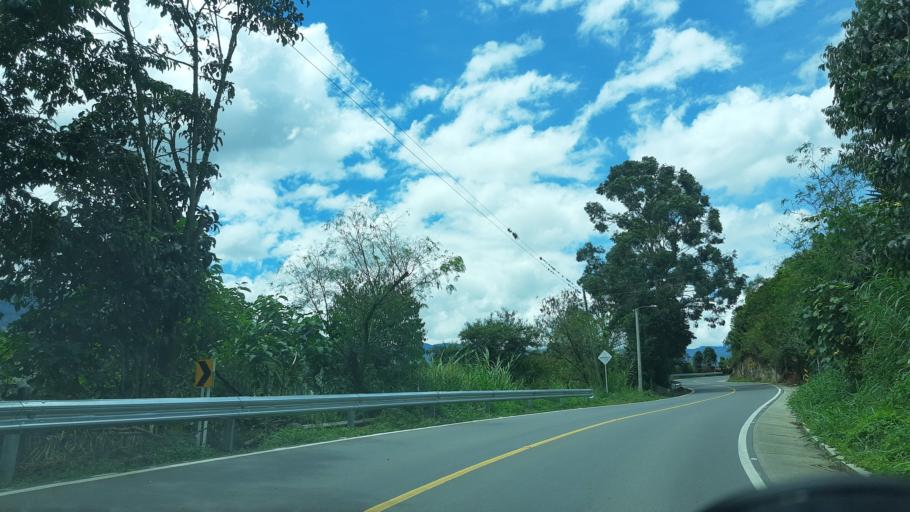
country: CO
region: Boyaca
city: Somondoco
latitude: 5.0083
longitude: -73.4363
